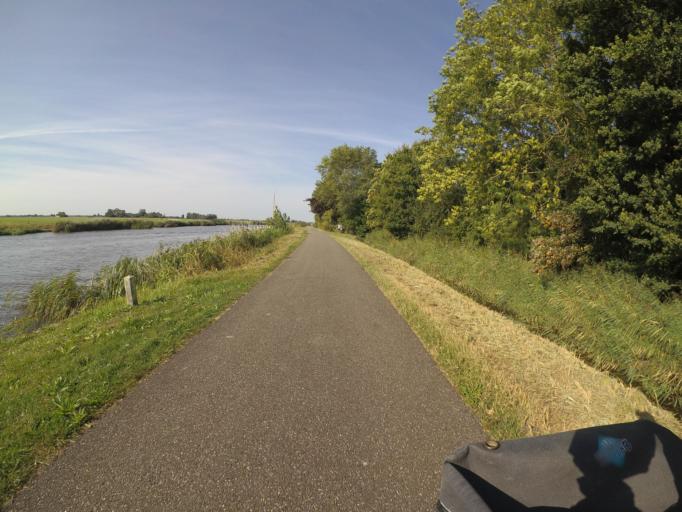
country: NL
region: Friesland
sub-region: Gemeente Dantumadiel
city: Rinsumageast
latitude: 53.3156
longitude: 5.9335
